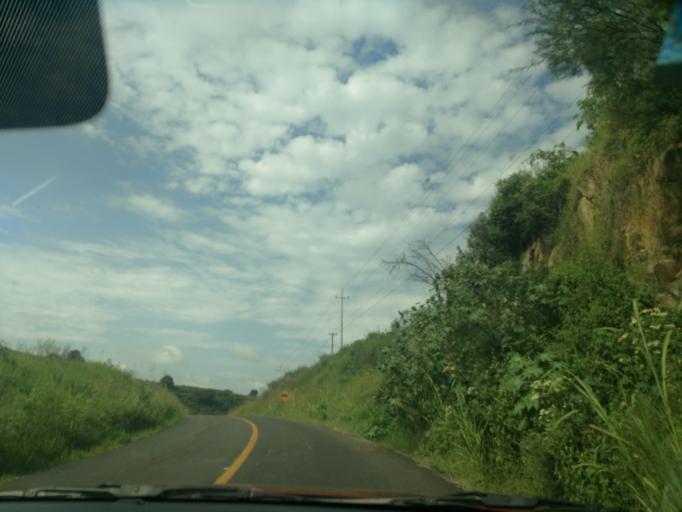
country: MX
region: Jalisco
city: El Salto
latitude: 20.4331
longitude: -104.4862
